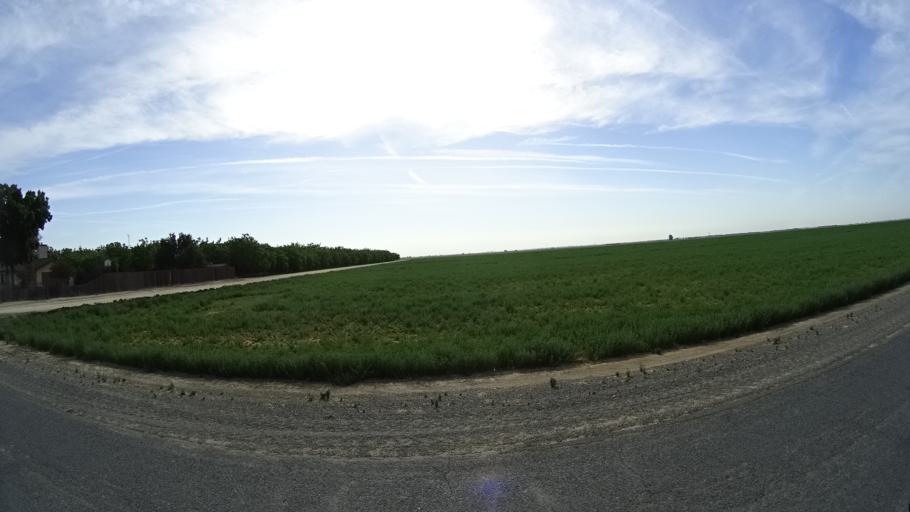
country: US
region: California
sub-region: Kings County
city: Hanford
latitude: 36.3683
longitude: -119.5470
